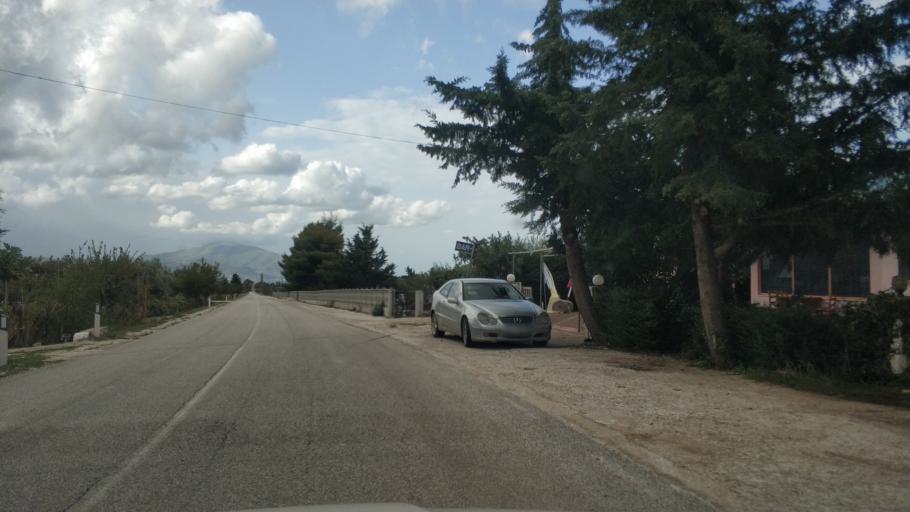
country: AL
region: Vlore
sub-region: Rrethi i Vlores
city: Orikum
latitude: 40.2719
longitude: 19.5124
